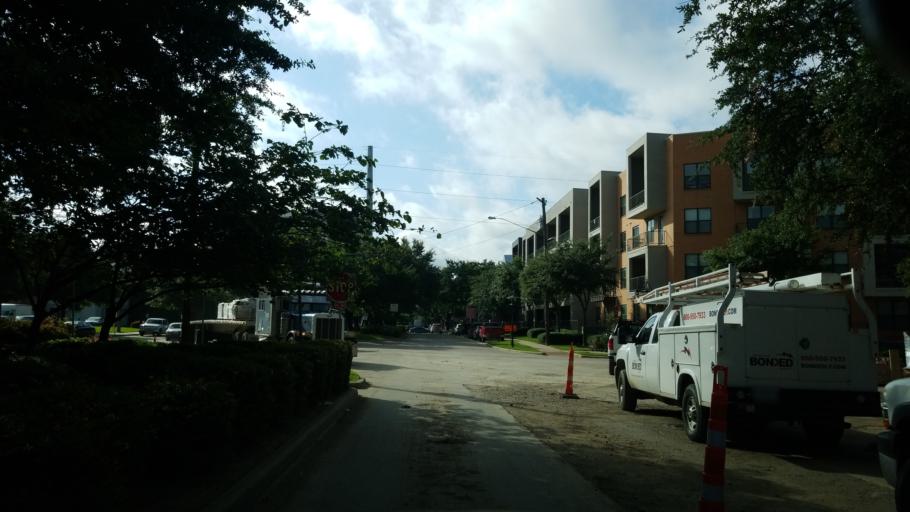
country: US
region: Texas
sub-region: Dallas County
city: Dallas
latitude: 32.7970
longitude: -96.8215
